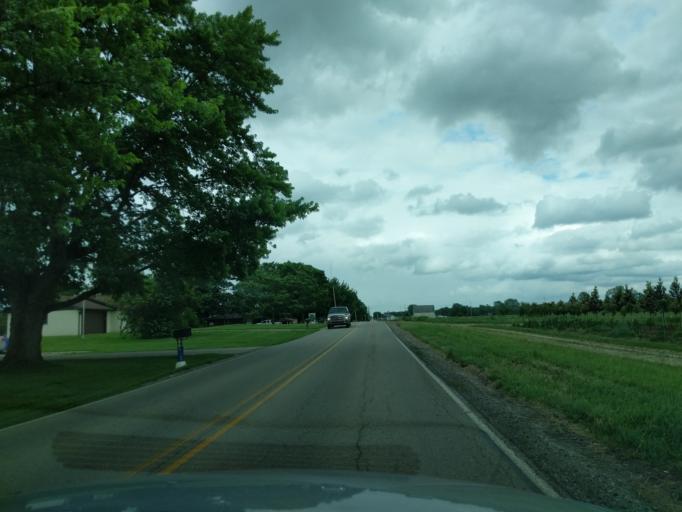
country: US
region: Indiana
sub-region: Madison County
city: Edgewood
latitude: 40.0612
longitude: -85.7262
